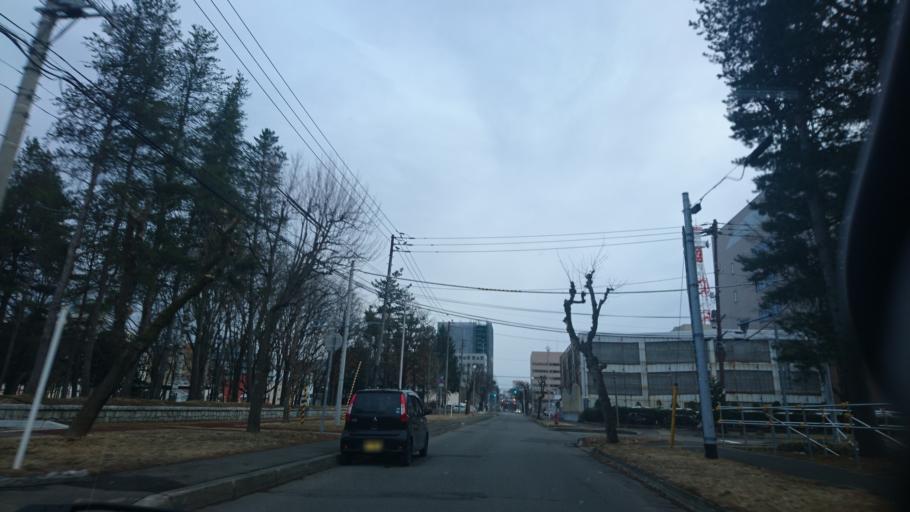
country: JP
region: Hokkaido
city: Obihiro
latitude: 42.9249
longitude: 143.1985
